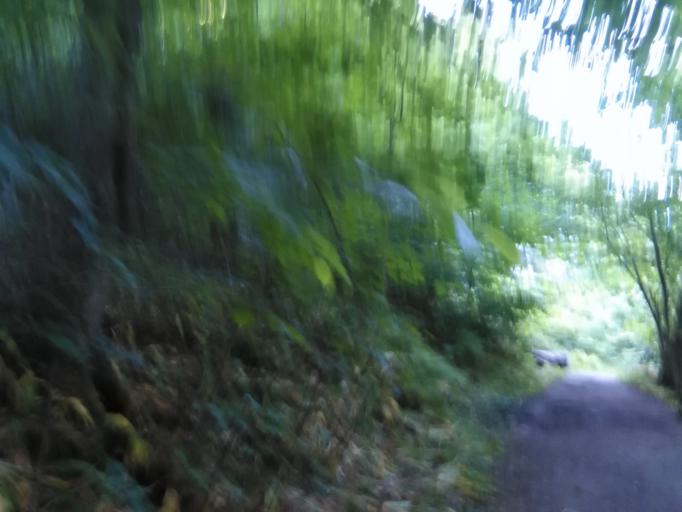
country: DK
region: Capital Region
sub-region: Bornholm Kommune
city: Akirkeby
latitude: 55.2240
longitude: 14.8795
